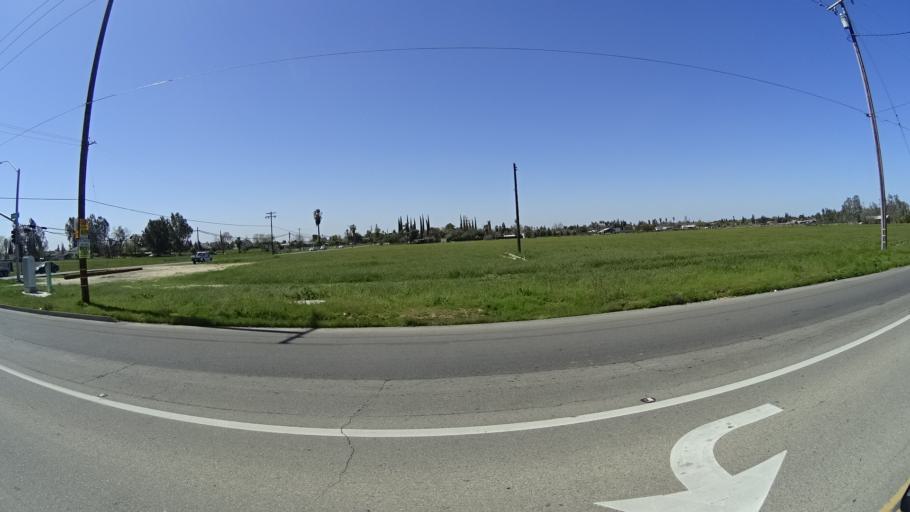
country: US
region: California
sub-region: Fresno County
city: West Park
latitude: 36.7796
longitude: -119.8711
